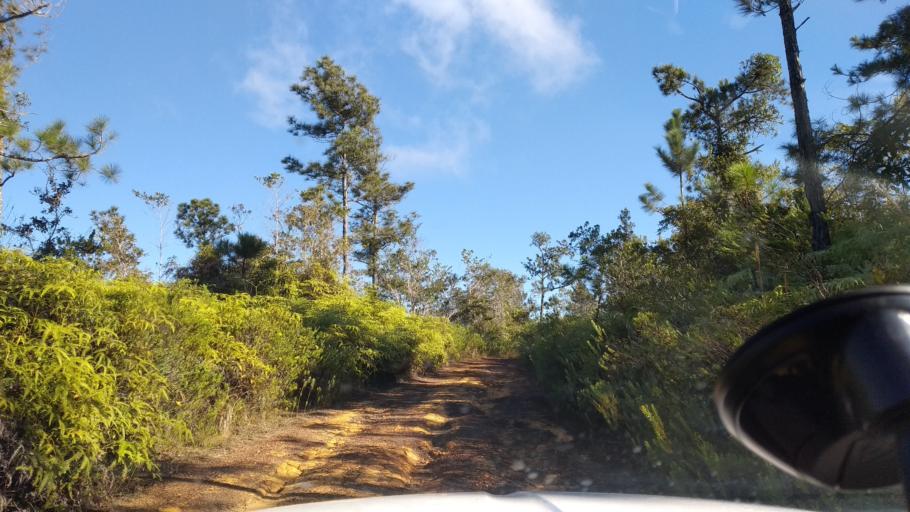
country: BZ
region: Cayo
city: Belmopan
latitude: 16.9981
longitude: -88.8486
